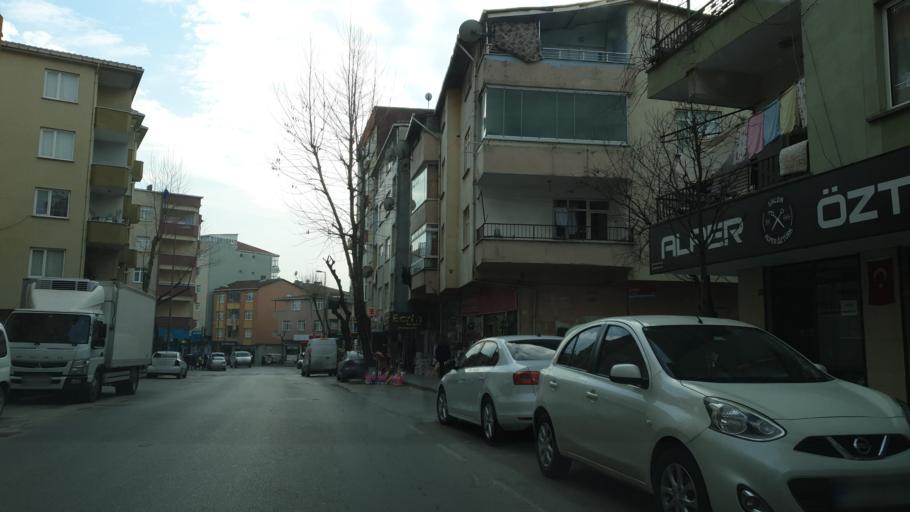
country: TR
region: Istanbul
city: Pendik
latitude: 40.8758
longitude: 29.2729
